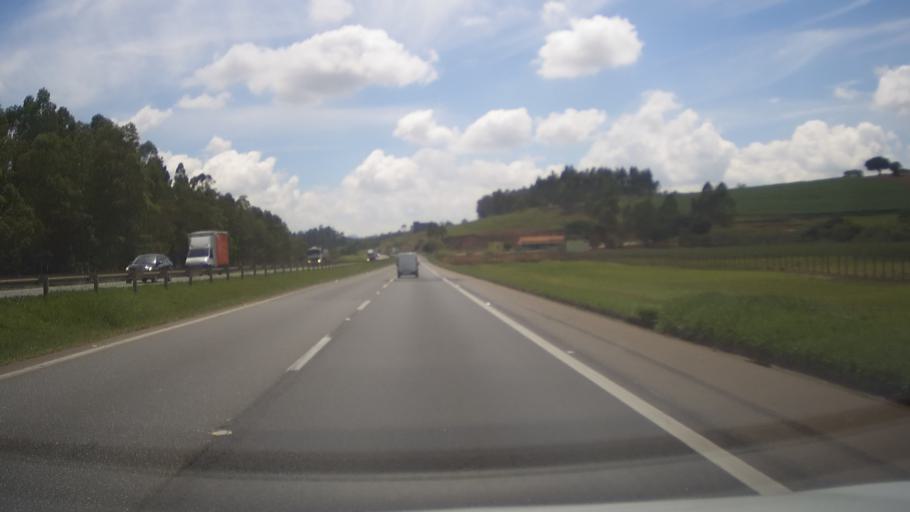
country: BR
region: Minas Gerais
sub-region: Santa Rita Do Sapucai
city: Santa Rita do Sapucai
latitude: -22.0957
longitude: -45.7141
